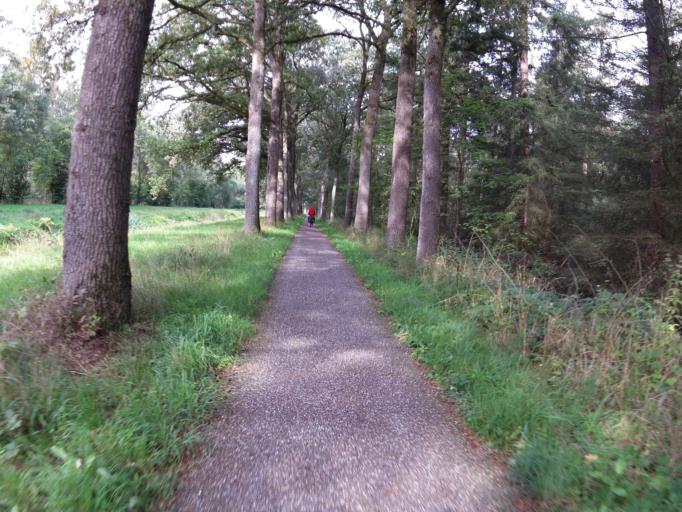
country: NL
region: Gelderland
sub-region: Oude IJsselstreek
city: Varsseveld
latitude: 51.9630
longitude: 6.4357
